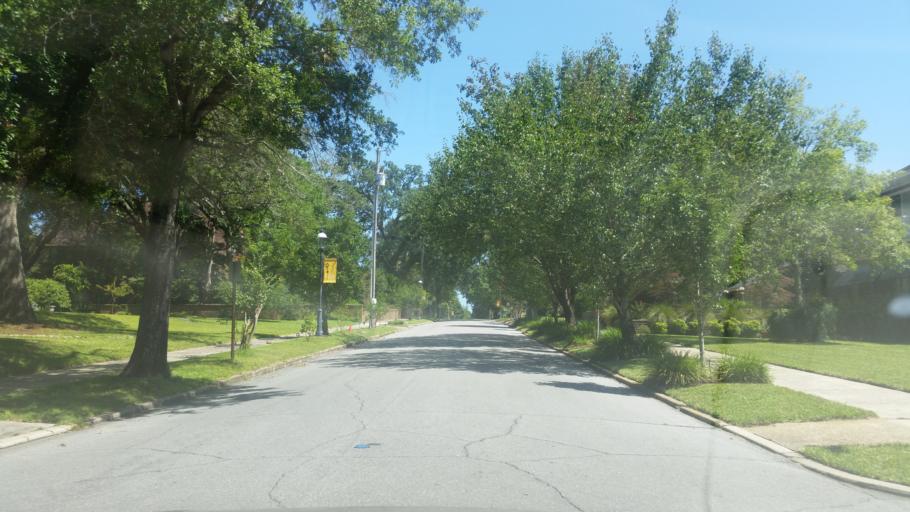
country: US
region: Florida
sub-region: Escambia County
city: Pensacola
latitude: 30.4237
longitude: -87.2207
